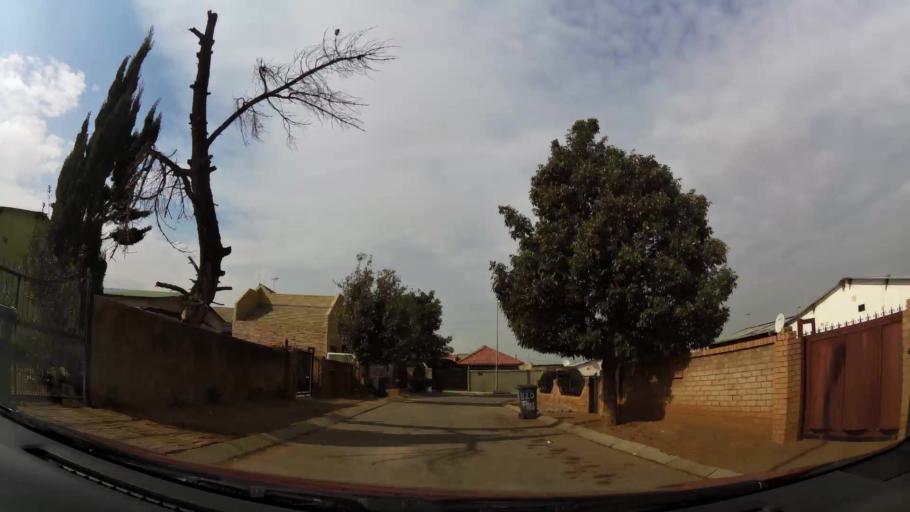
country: ZA
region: Gauteng
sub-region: City of Johannesburg Metropolitan Municipality
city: Soweto
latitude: -26.2614
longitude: 27.8226
